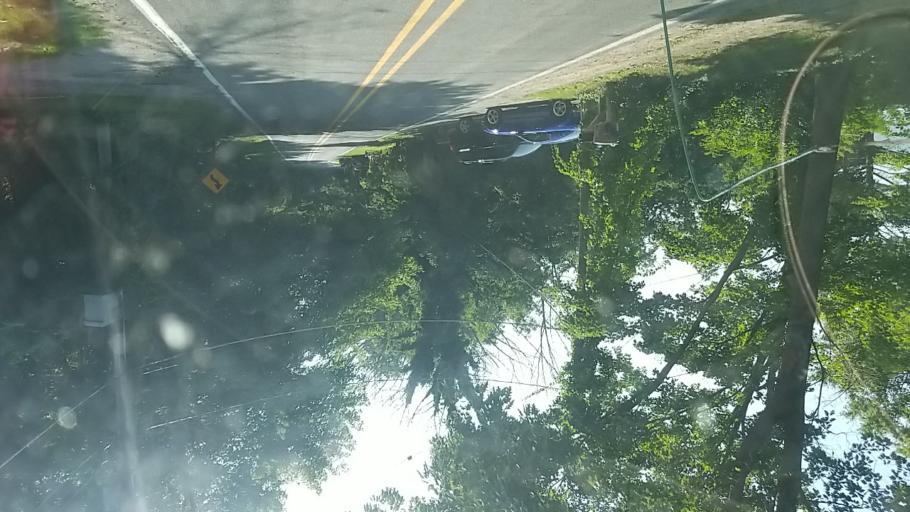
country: US
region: Michigan
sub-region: Muskegon County
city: Montague
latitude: 43.3661
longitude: -86.3957
